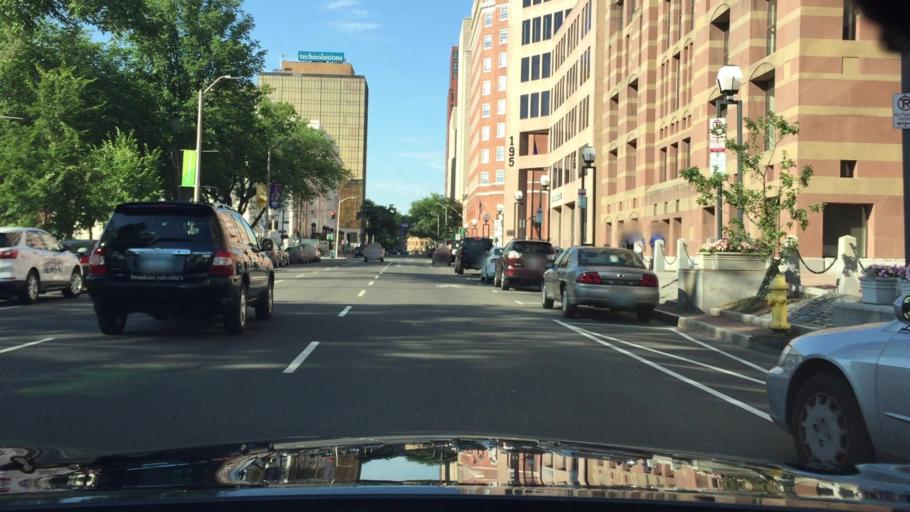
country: US
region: Connecticut
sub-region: New Haven County
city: New Haven
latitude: 41.3073
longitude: -72.9248
